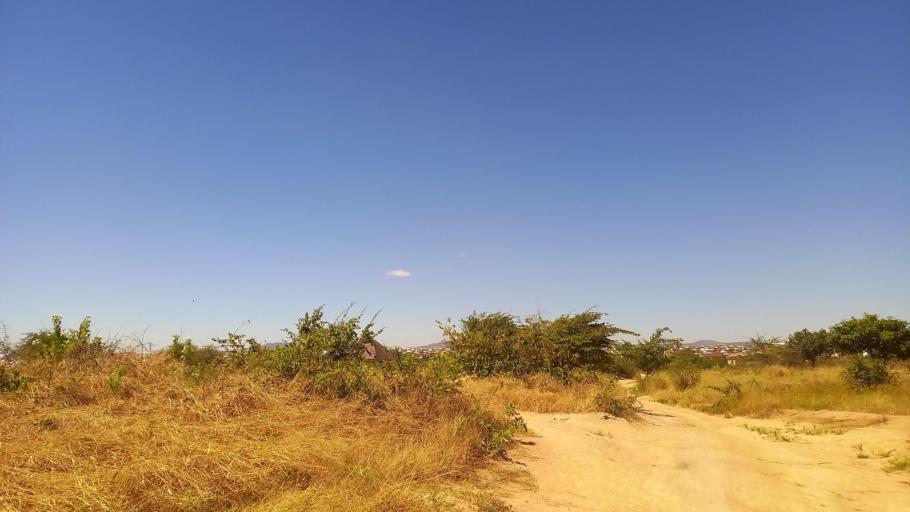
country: TZ
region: Dodoma
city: Dodoma
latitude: -6.1167
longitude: 35.6965
